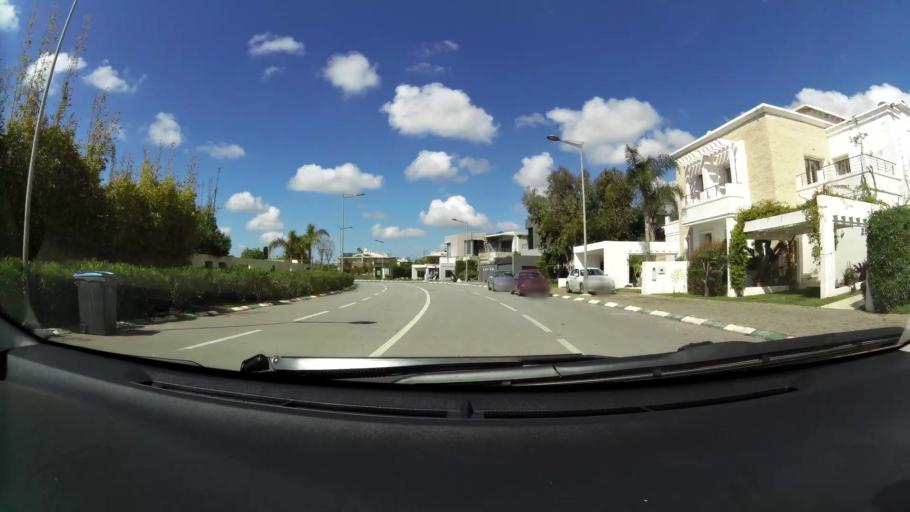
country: MA
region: Grand Casablanca
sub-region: Nouaceur
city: Bouskoura
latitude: 33.4684
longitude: -7.6018
